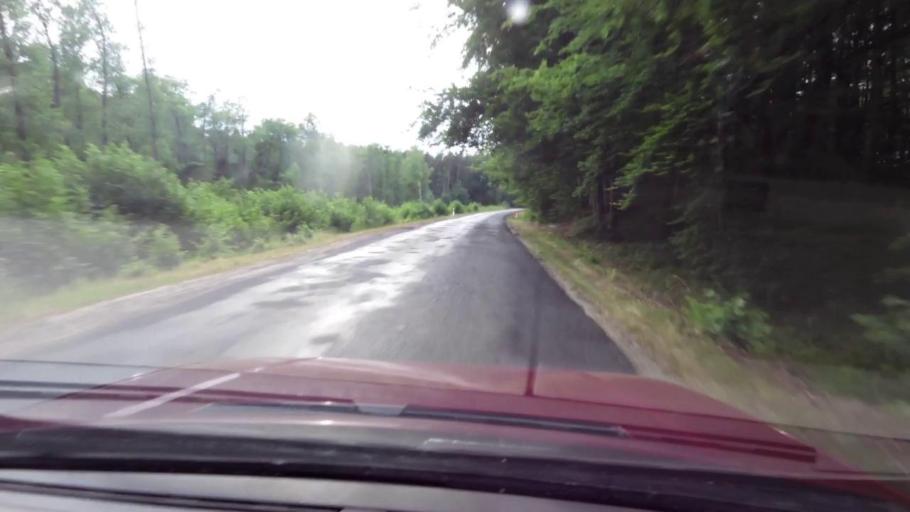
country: PL
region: Pomeranian Voivodeship
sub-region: Powiat slupski
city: Kepice
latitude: 54.2692
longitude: 16.9963
